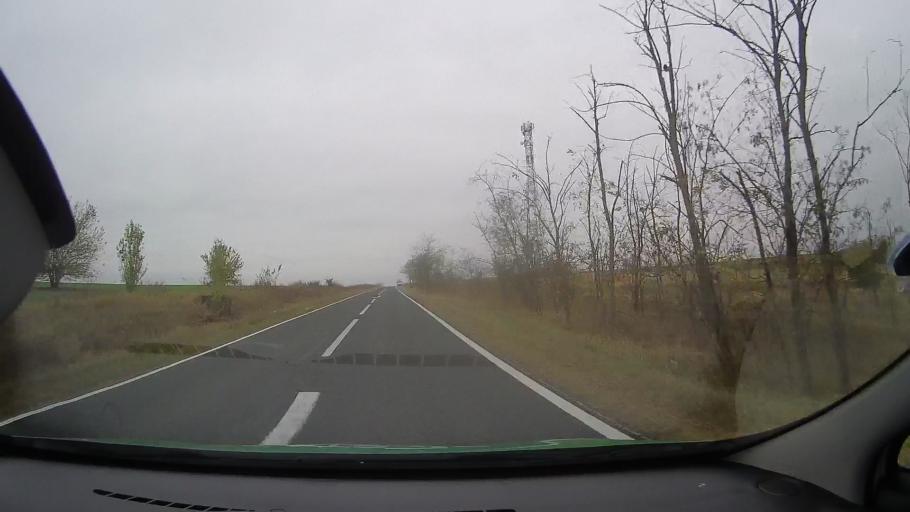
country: RO
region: Constanta
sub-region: Comuna Saraiu
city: Saraiu
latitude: 44.7113
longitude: 28.1213
